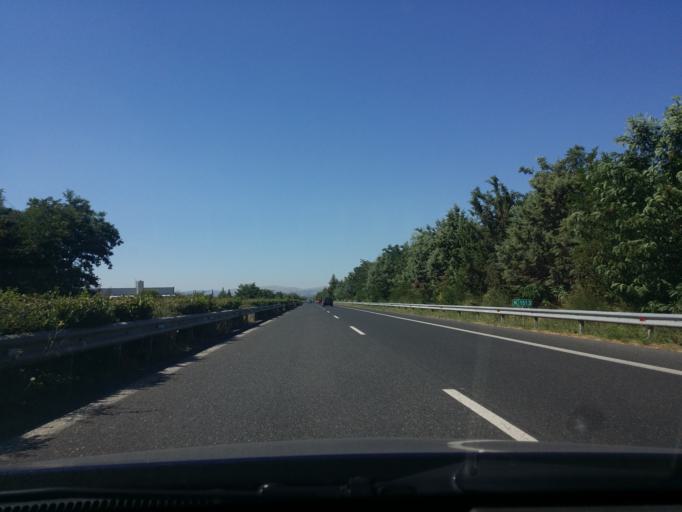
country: GR
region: Peloponnese
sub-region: Nomos Arkadias
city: Tripoli
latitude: 37.5639
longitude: 22.4249
